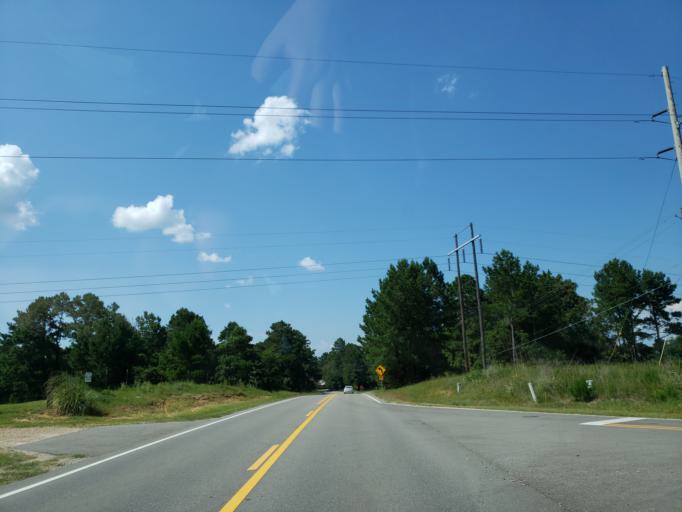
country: US
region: Mississippi
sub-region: Lamar County
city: Sumrall
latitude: 31.3985
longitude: -89.5419
